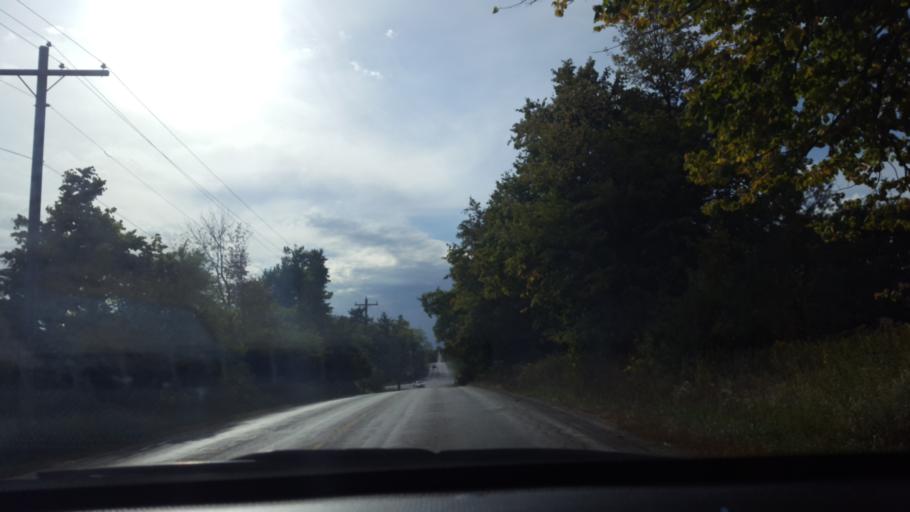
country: CA
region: Ontario
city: Vaughan
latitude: 43.9004
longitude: -79.5713
